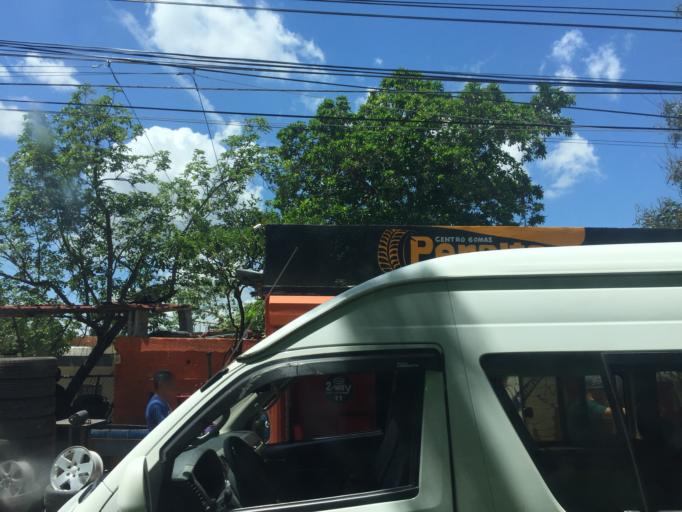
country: DO
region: Santiago
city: Santiago de los Caballeros
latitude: 19.4417
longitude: -70.7131
